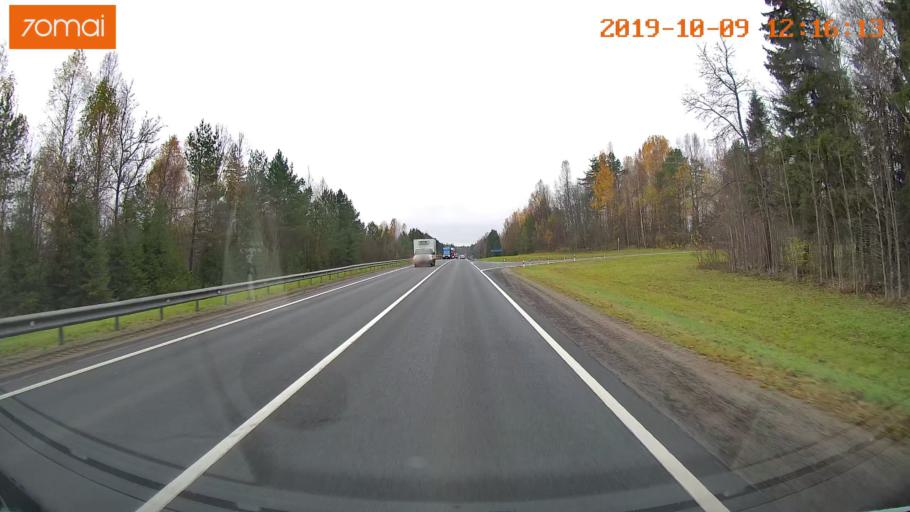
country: RU
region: Jaroslavl
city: Prechistoye
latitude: 58.4718
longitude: 40.3215
